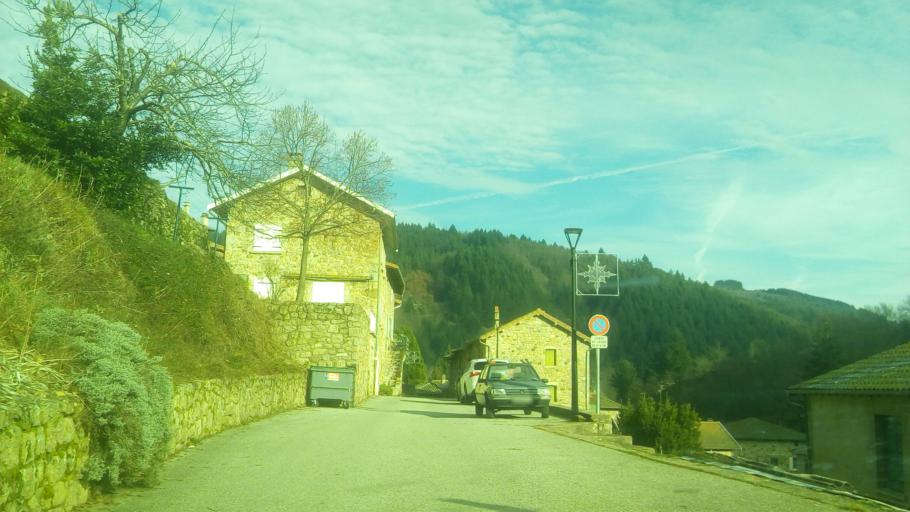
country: FR
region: Rhone-Alpes
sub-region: Departement de l'Ardeche
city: Saint-Martin-de-Valamas
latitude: 44.8875
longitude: 4.3748
